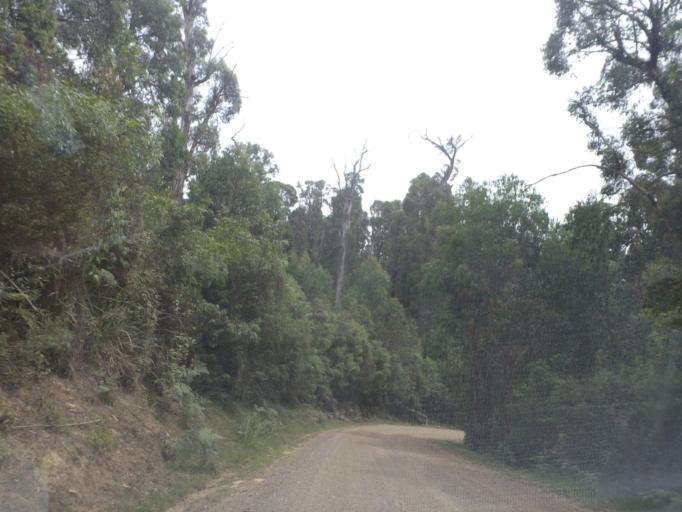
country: AU
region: Victoria
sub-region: Yarra Ranges
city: Healesville
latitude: -37.4527
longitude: 145.5728
